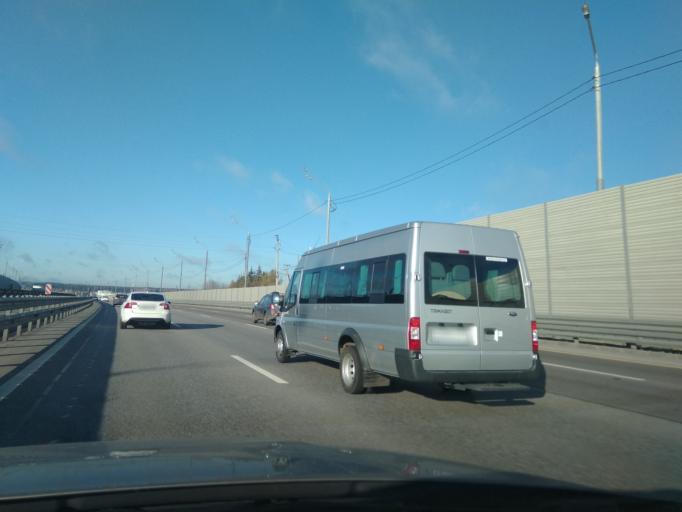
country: RU
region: Moskovskaya
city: Rozhdestveno
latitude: 55.8190
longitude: 37.0113
